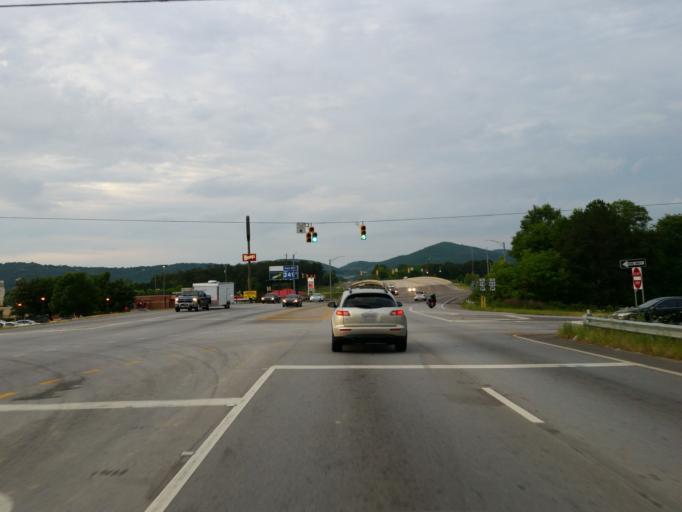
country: US
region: Alabama
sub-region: Calhoun County
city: Oxford
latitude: 33.6119
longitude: -85.7863
